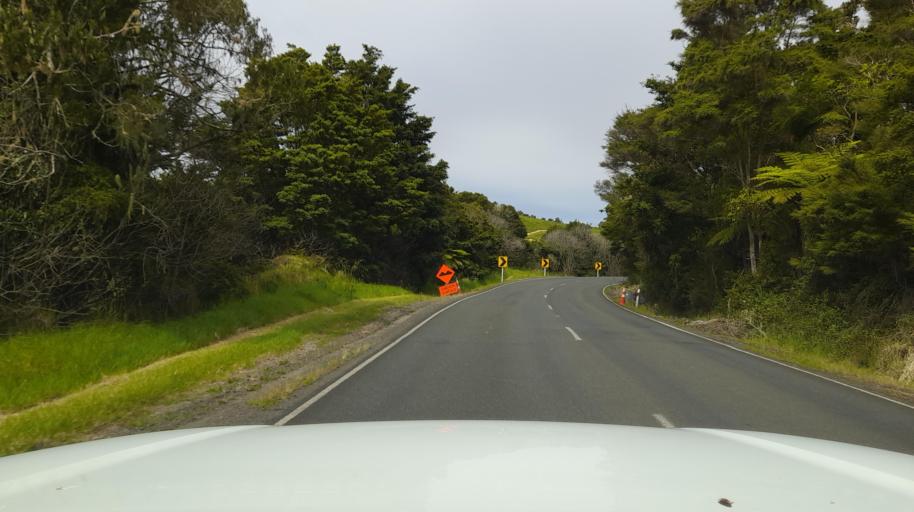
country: NZ
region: Northland
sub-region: Far North District
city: Kaitaia
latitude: -35.2710
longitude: 173.4850
